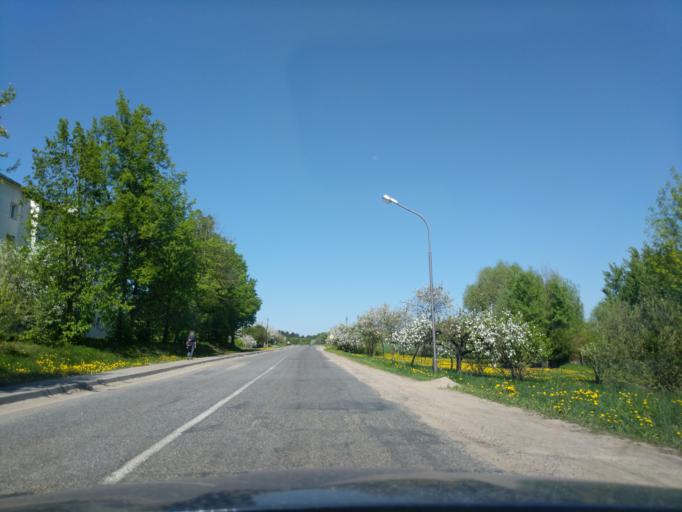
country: BY
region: Minsk
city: Myadzyel
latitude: 54.8886
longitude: 26.9149
